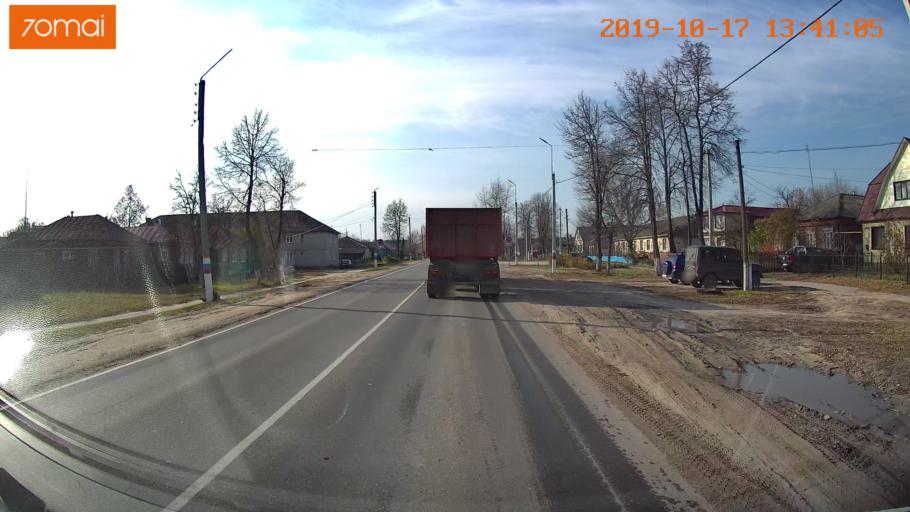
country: RU
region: Rjazan
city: Tuma
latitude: 55.1490
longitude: 40.5684
